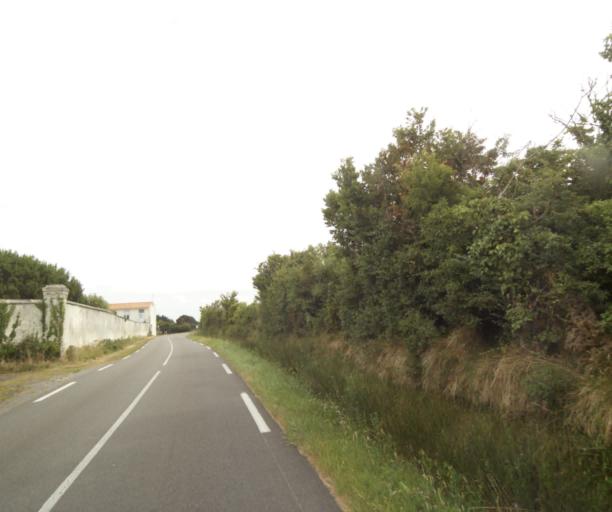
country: FR
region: Pays de la Loire
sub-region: Departement de la Vendee
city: Chateau-d'Olonne
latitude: 46.4683
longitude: -1.7286
